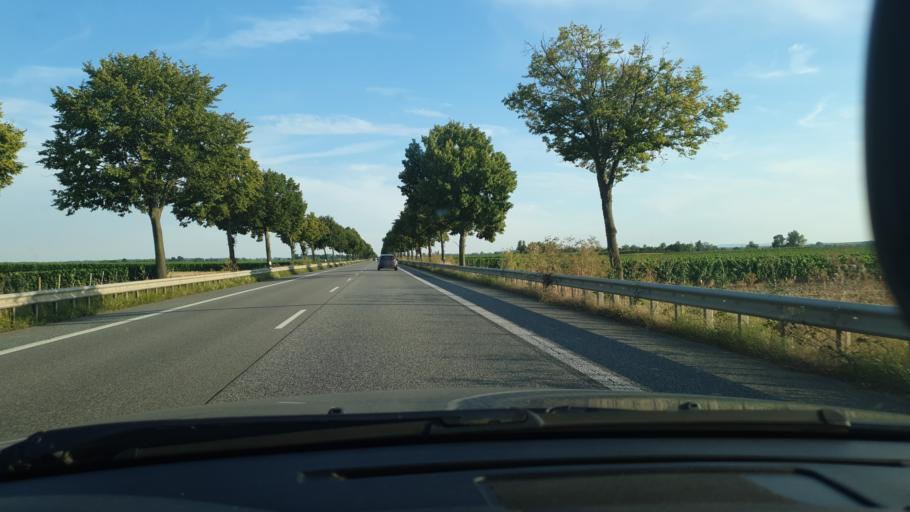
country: DE
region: Rheinland-Pfalz
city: Alsheim
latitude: 49.7598
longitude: 8.3523
